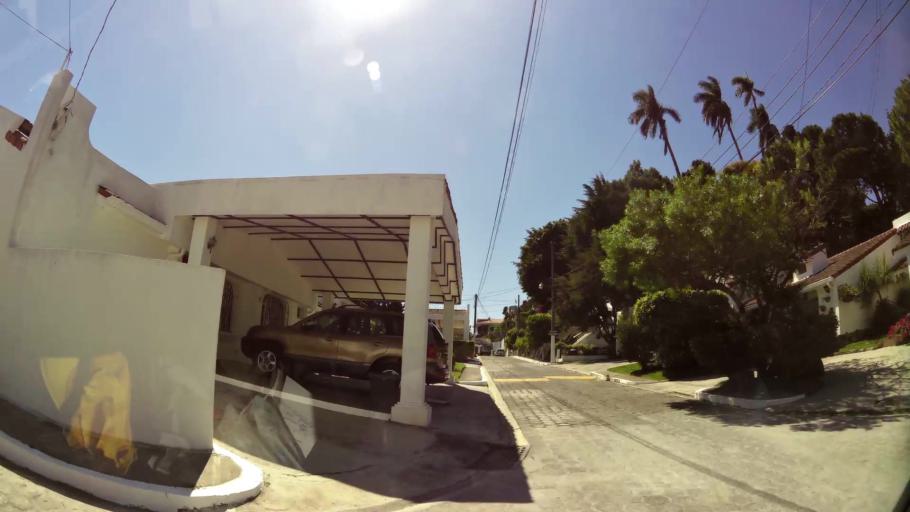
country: SV
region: La Libertad
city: Nuevo Cuscatlan
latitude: 13.6501
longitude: -89.2797
